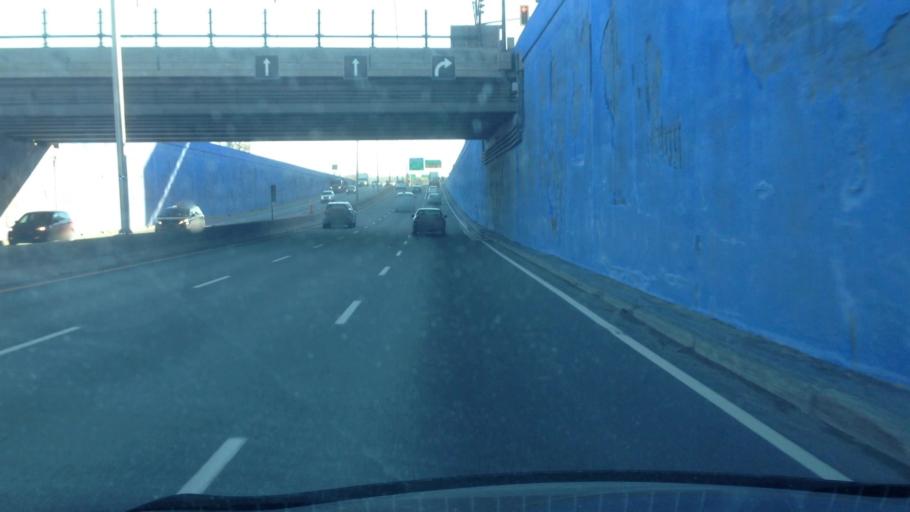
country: CA
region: Quebec
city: Montreal-Ouest
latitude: 45.4446
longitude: -73.6643
